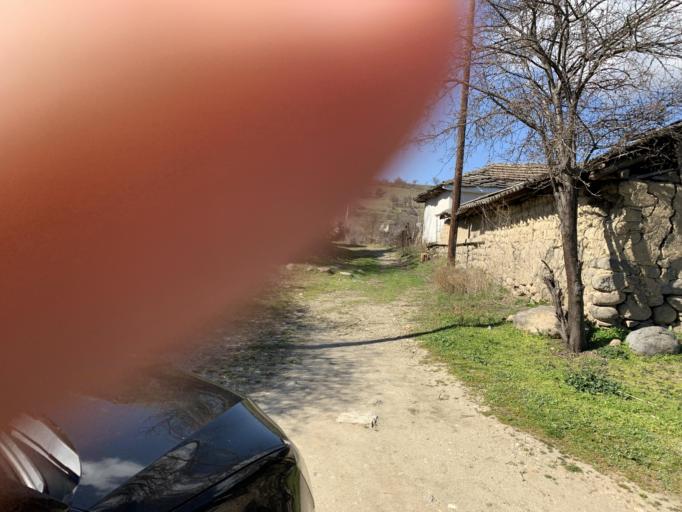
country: MK
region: Demir Kapija
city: Demir Kapija
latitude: 41.4192
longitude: 22.1658
